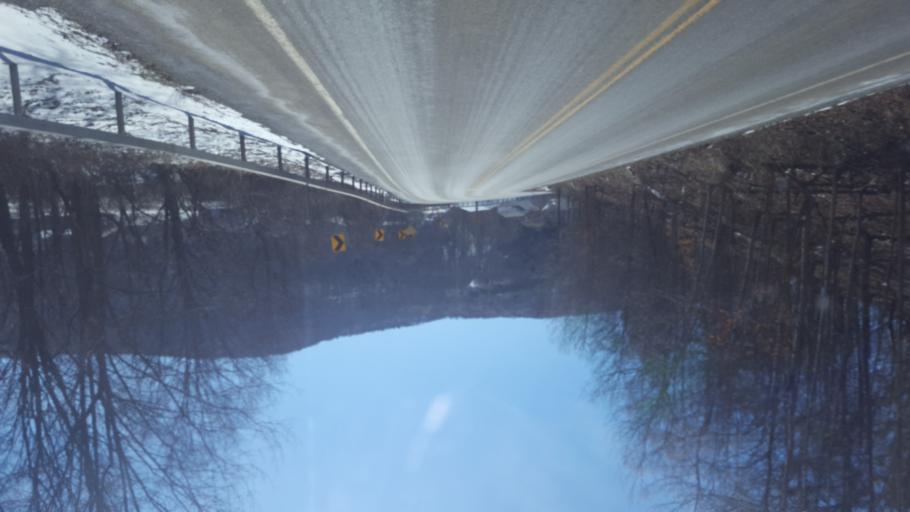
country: US
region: New York
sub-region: Allegany County
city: Andover
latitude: 42.0389
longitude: -77.7846
